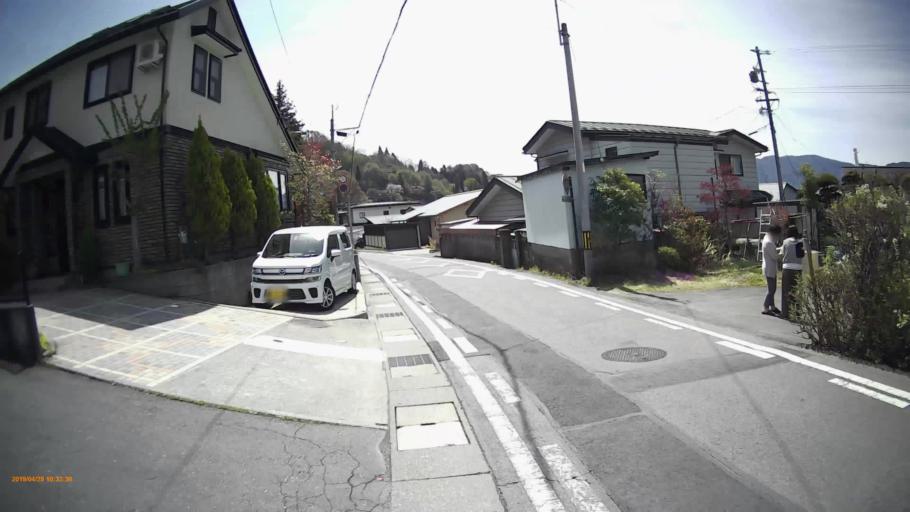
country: JP
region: Nagano
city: Suwa
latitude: 36.0553
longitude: 138.1166
